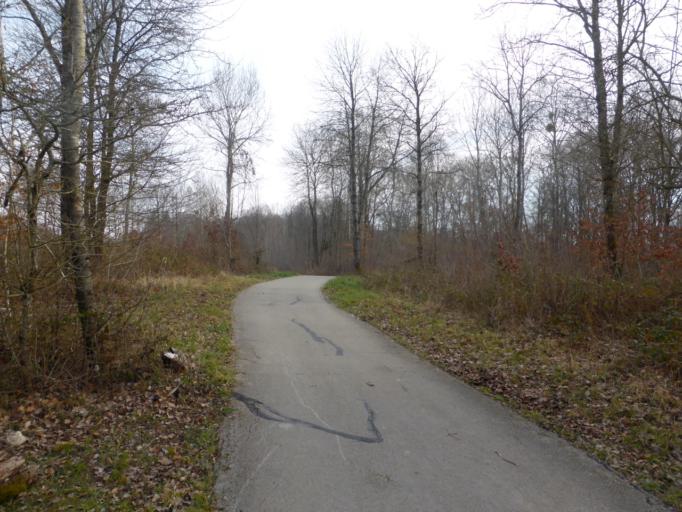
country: FR
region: Champagne-Ardenne
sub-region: Departement de l'Aube
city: Lusigny-sur-Barse
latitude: 48.2745
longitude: 4.3019
